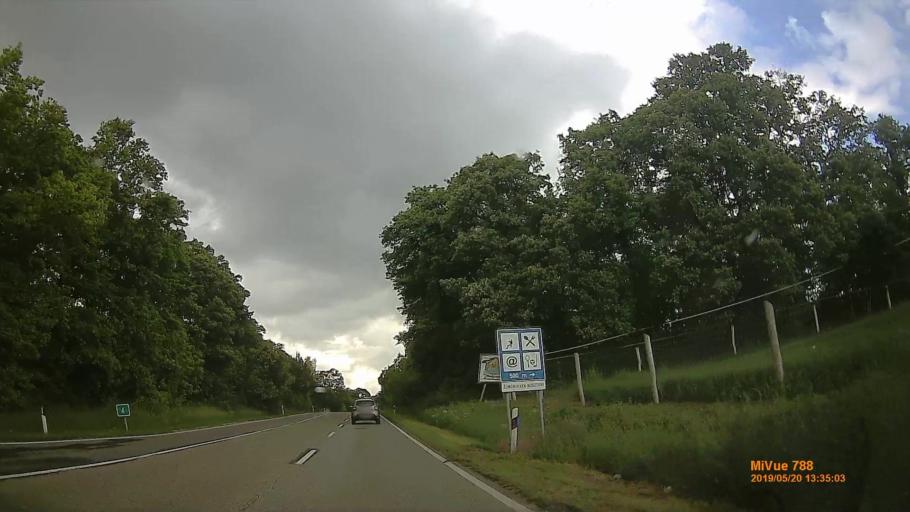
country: HU
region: Veszprem
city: Csopak
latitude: 47.0007
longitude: 17.9151
